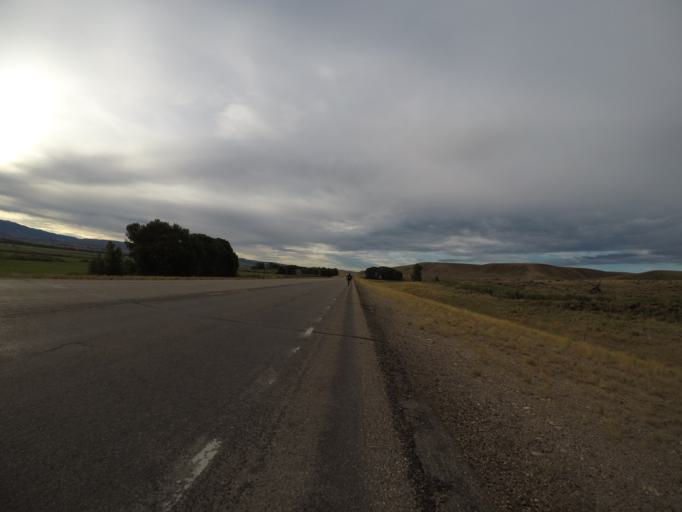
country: US
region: Wyoming
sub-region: Carbon County
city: Saratoga
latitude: 41.4113
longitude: -106.7816
